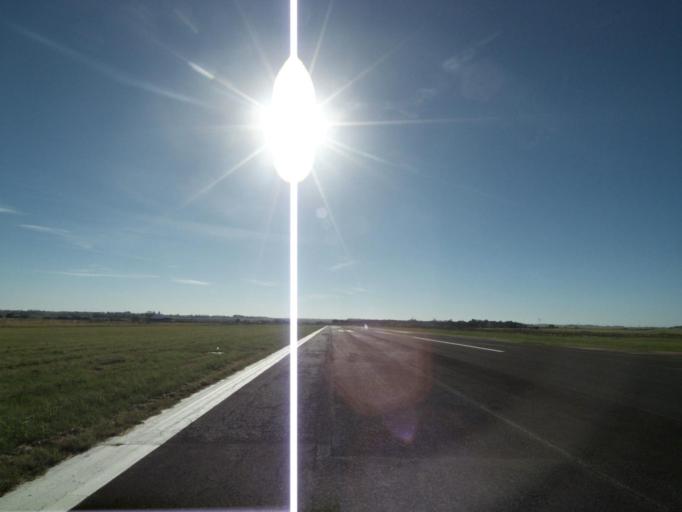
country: BR
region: Rio Grande do Sul
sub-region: Uruguaiana
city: Uruguaiana
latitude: -29.7817
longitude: -57.0361
